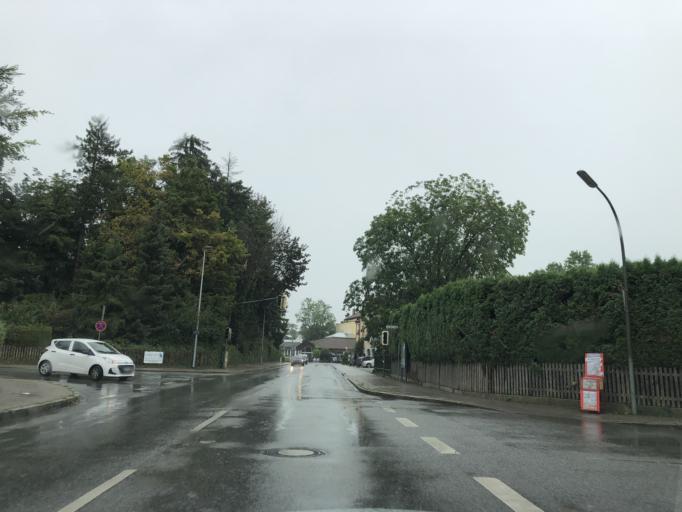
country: DE
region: Bavaria
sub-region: Upper Bavaria
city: Erding
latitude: 48.3025
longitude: 11.8985
